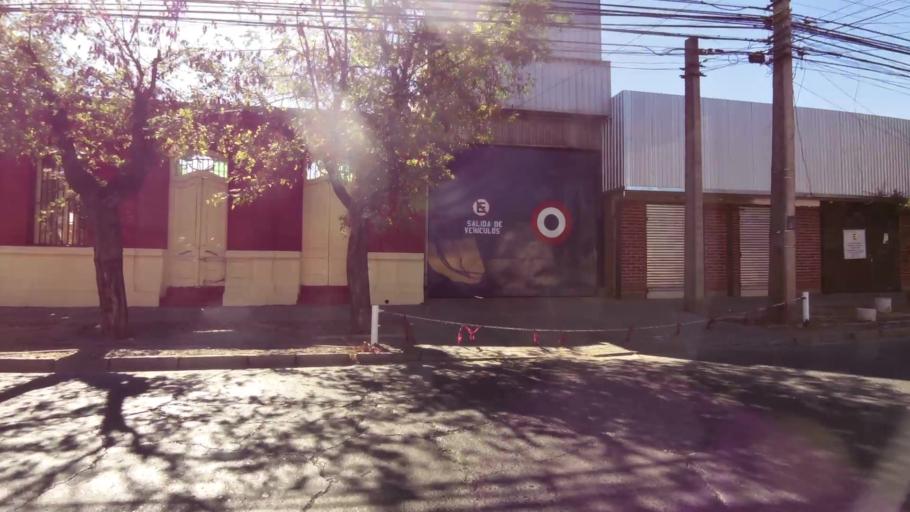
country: CL
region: O'Higgins
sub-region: Provincia de Cachapoal
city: Rancagua
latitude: -34.1667
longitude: -70.7470
